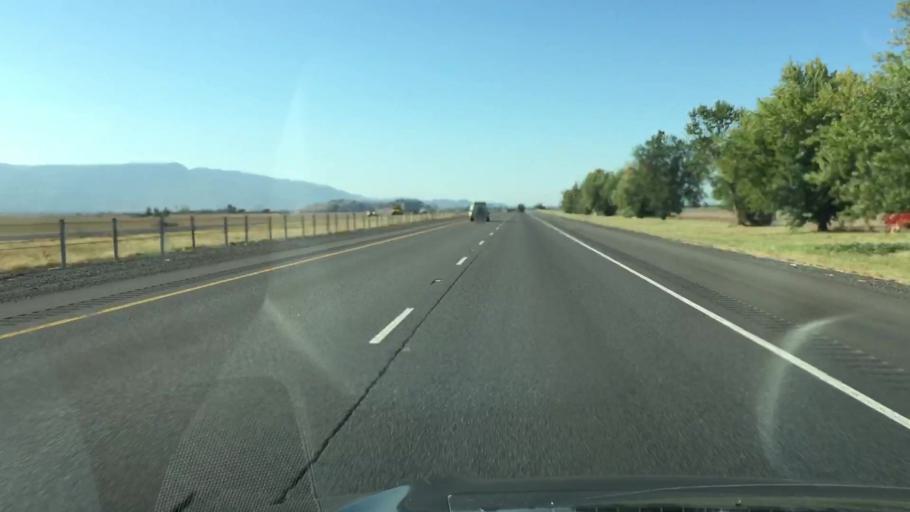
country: US
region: Oregon
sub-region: Linn County
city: Brownsville
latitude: 44.3573
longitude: -123.0617
